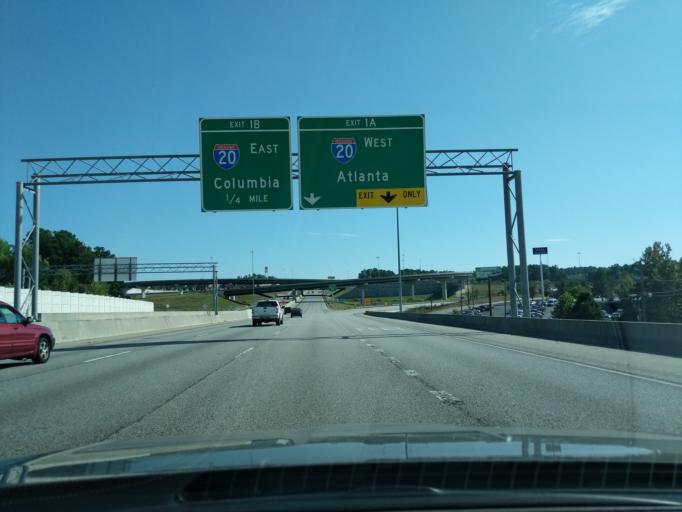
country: US
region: Georgia
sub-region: Columbia County
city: Martinez
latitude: 33.4974
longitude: -82.0860
